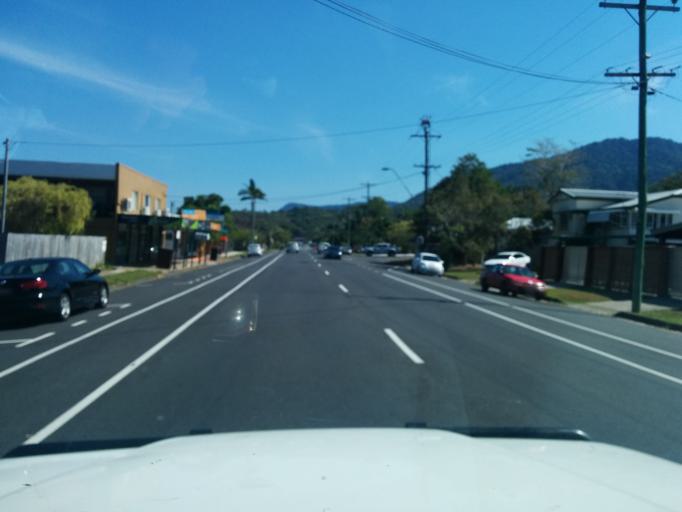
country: AU
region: Queensland
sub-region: Cairns
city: Redlynch
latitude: -16.9039
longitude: 145.7288
